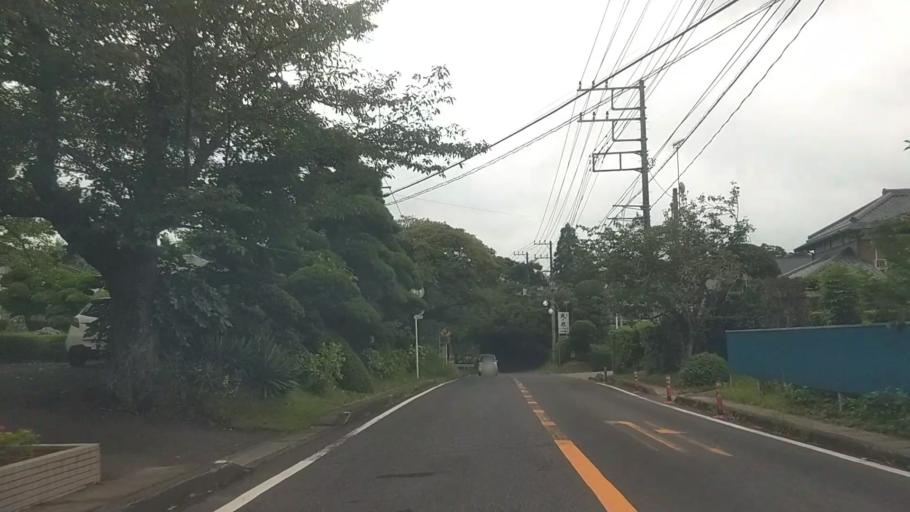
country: JP
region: Chiba
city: Kisarazu
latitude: 35.3013
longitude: 140.0732
